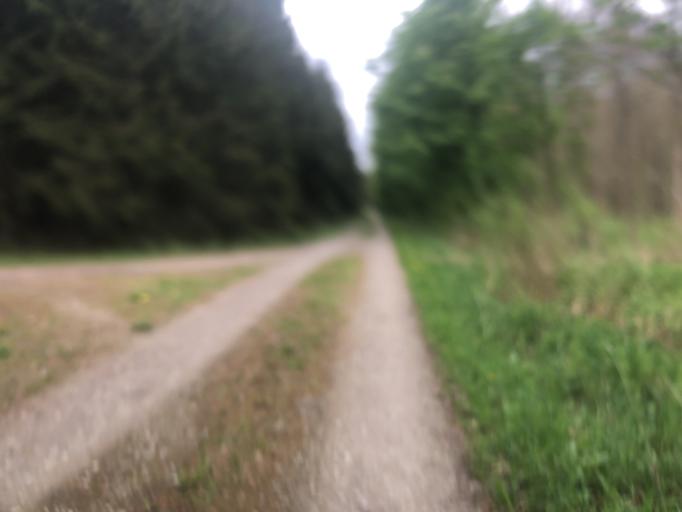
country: DK
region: Zealand
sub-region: Koge Kommune
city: Ejby
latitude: 55.4426
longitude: 12.0920
